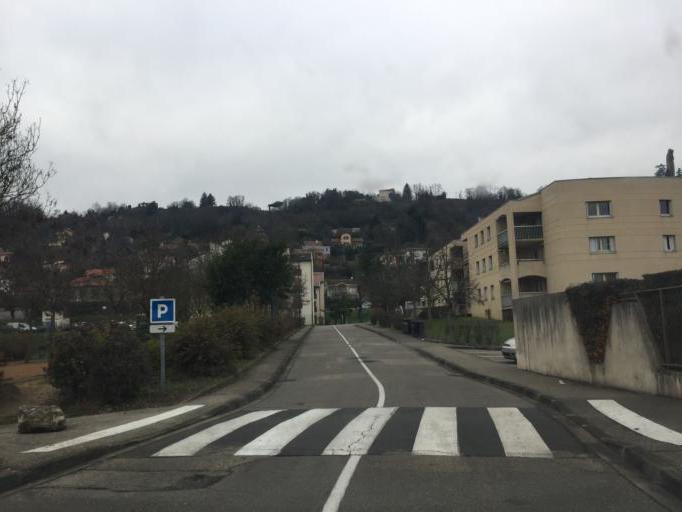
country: FR
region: Rhone-Alpes
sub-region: Departement de l'Ain
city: Miribel
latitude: 45.8242
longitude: 4.9500
